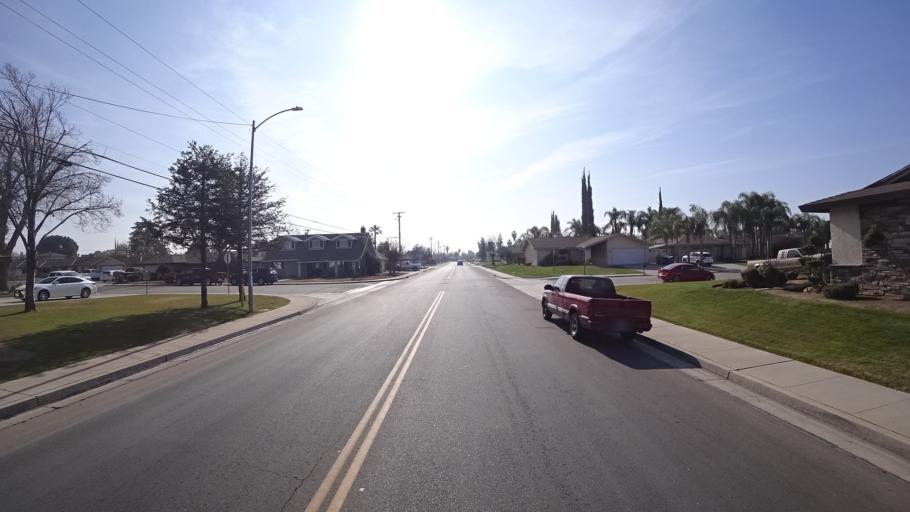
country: US
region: California
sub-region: Kern County
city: Bakersfield
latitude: 35.3277
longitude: -119.0434
